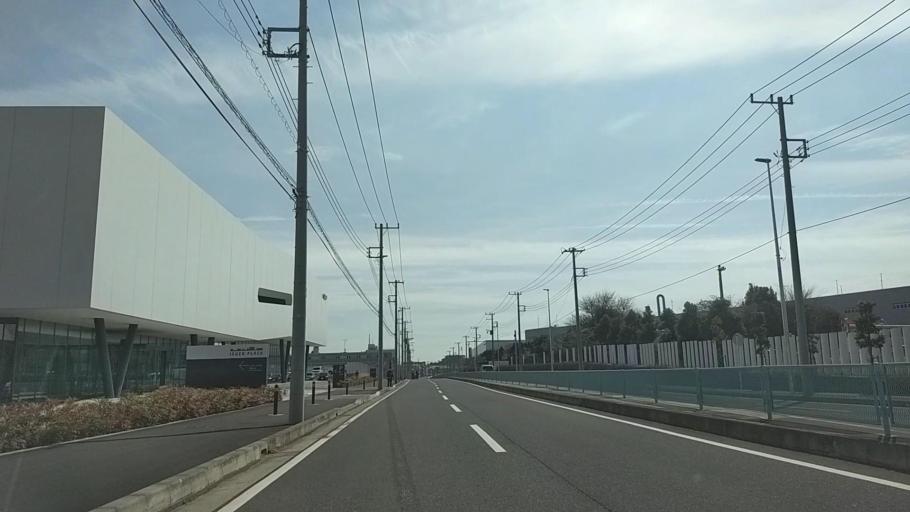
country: JP
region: Kanagawa
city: Fujisawa
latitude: 35.3996
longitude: 139.4562
